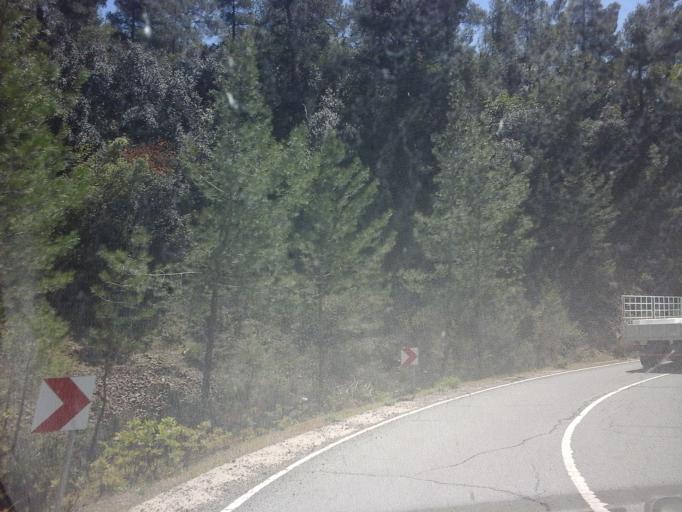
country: CY
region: Lefkosia
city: Kakopetria
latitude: 34.9953
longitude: 32.7927
